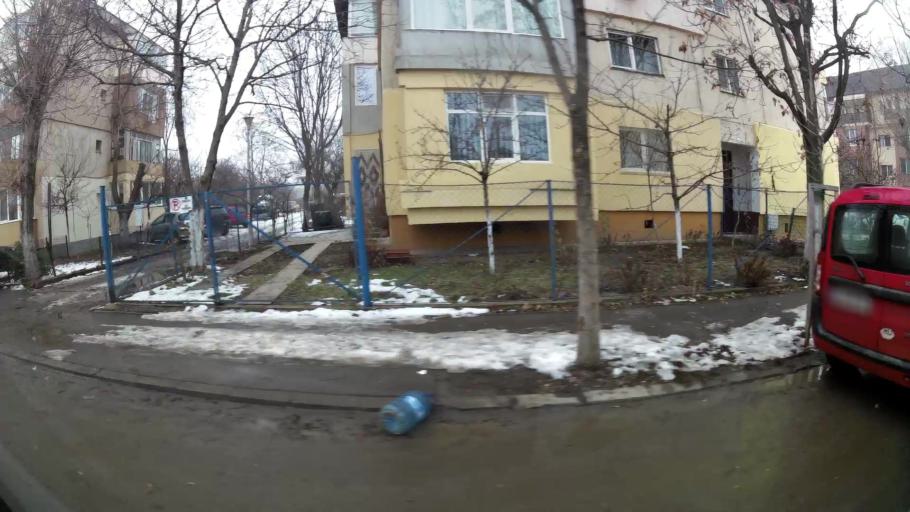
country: RO
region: Ilfov
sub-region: Comuna Chiajna
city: Rosu
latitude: 44.4387
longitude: 26.0036
